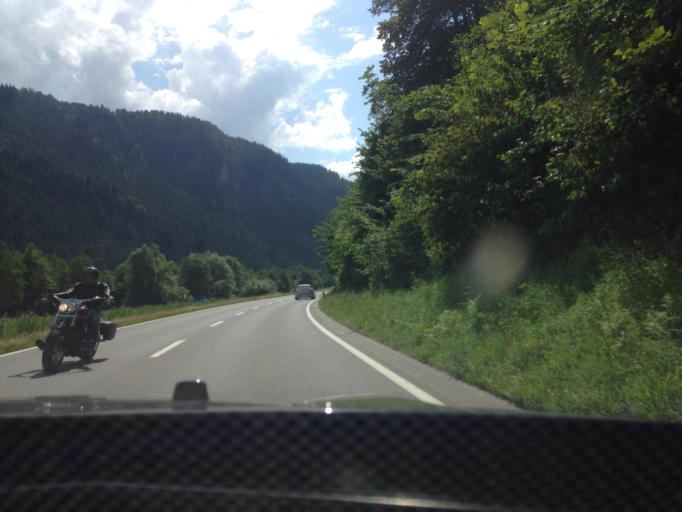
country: CH
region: Grisons
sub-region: Surselva District
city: Breil
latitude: 46.7623
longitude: 9.0961
